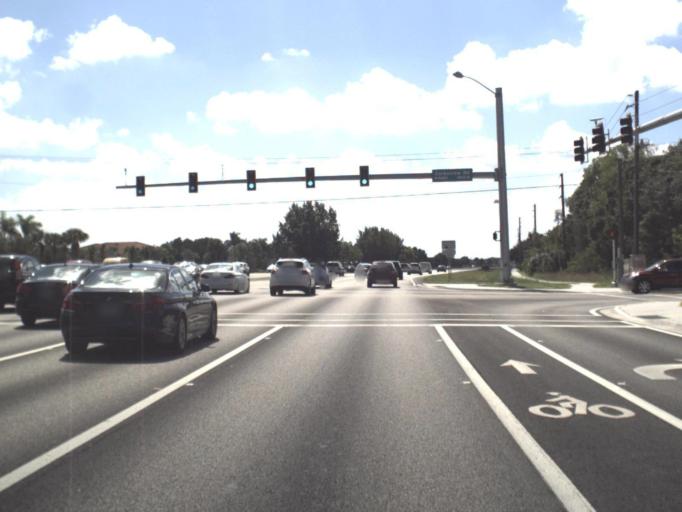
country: US
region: Florida
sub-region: Lee County
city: Estero
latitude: 26.4318
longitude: -81.8108
